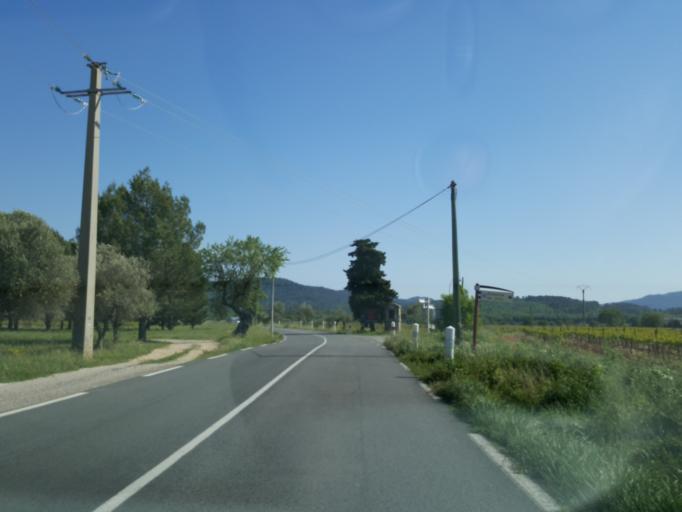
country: FR
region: Provence-Alpes-Cote d'Azur
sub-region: Departement du Var
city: La Roquebrussanne
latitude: 43.3269
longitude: 5.9833
